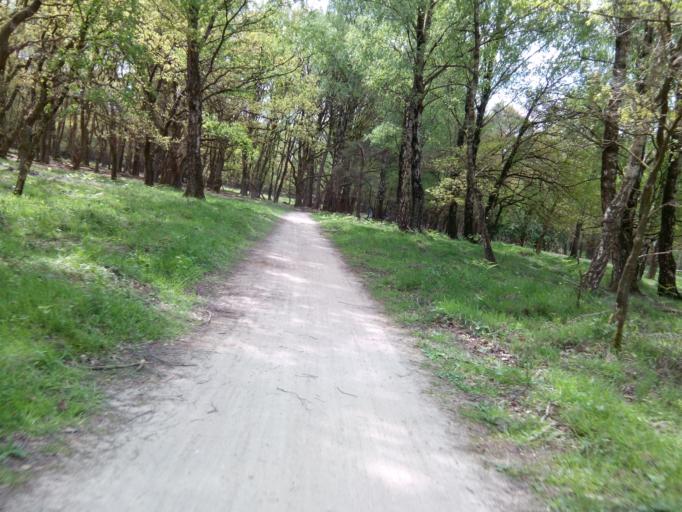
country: NL
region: Gelderland
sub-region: Gemeente Renkum
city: Wolfheze
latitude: 52.0459
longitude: 5.7757
